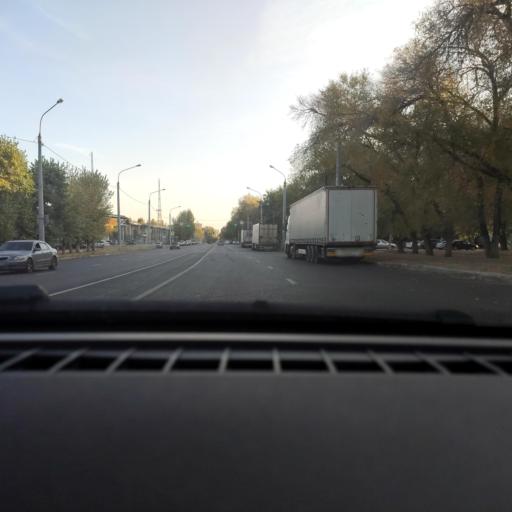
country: RU
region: Voronezj
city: Maslovka
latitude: 51.6056
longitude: 39.2438
